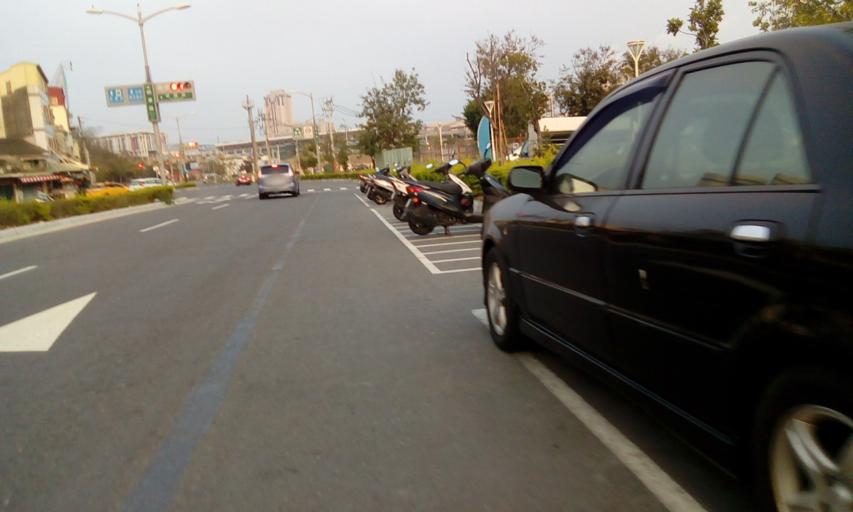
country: TW
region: Kaohsiung
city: Kaohsiung
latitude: 22.6890
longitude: 120.3010
